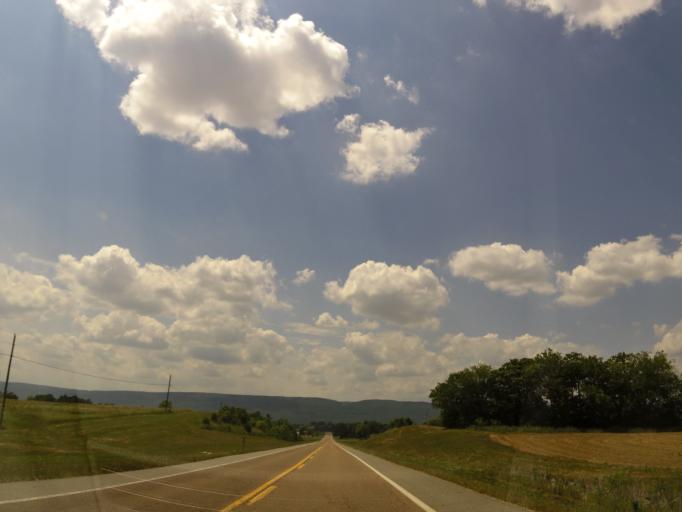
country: US
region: Tennessee
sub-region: Bledsoe County
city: Pikeville
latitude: 35.5852
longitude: -85.1744
